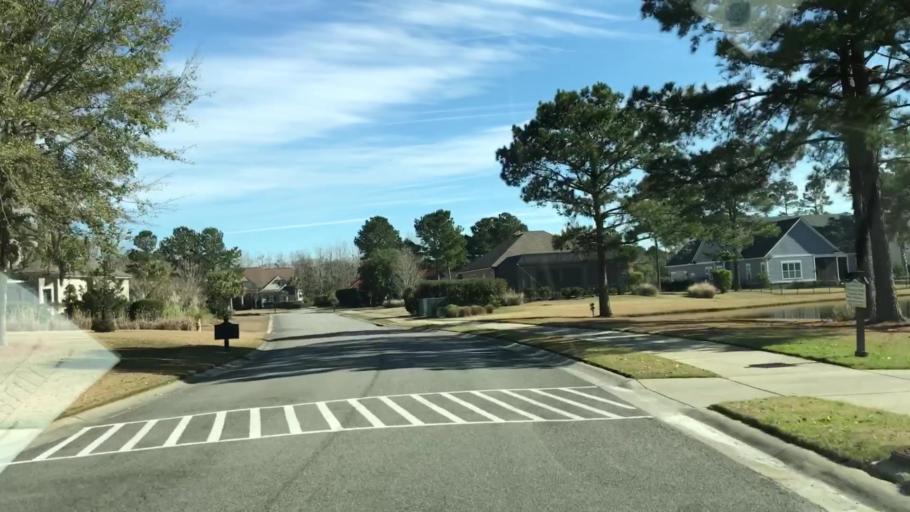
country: US
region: South Carolina
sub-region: Beaufort County
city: Bluffton
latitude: 32.2505
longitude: -80.9146
